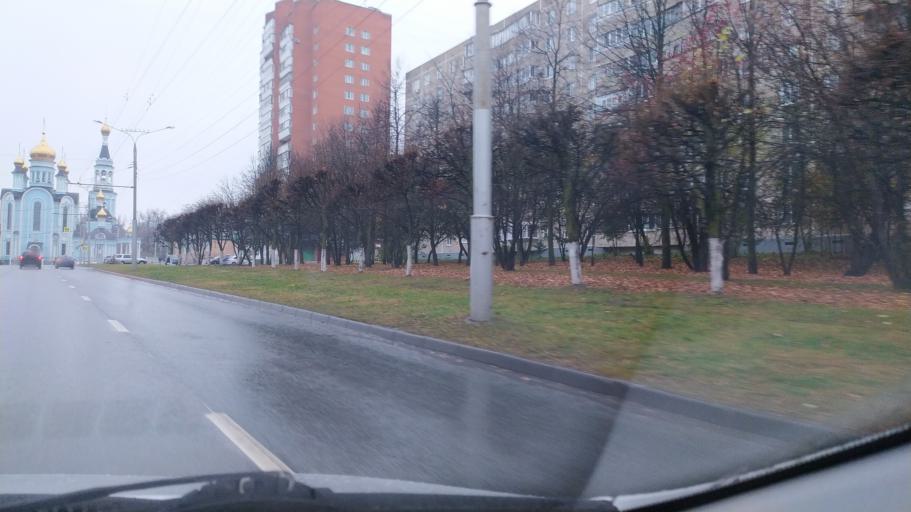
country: RU
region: Chuvashia
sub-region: Cheboksarskiy Rayon
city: Cheboksary
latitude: 56.1427
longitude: 47.1859
